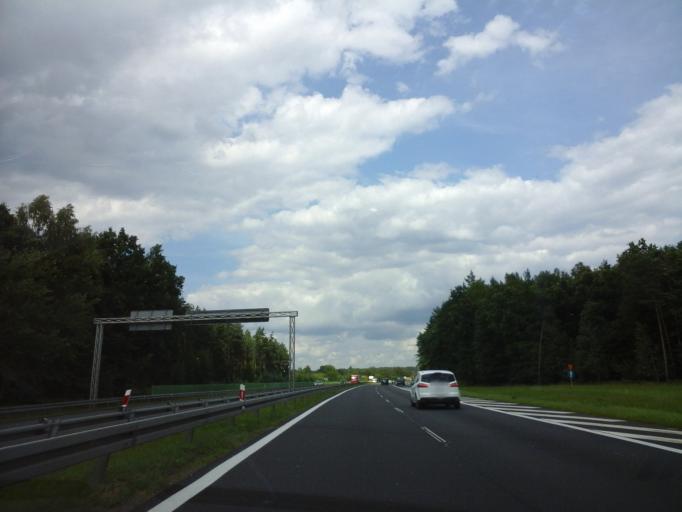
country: PL
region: West Pomeranian Voivodeship
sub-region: Powiat goleniowski
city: Goleniow
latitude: 53.5718
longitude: 14.8002
